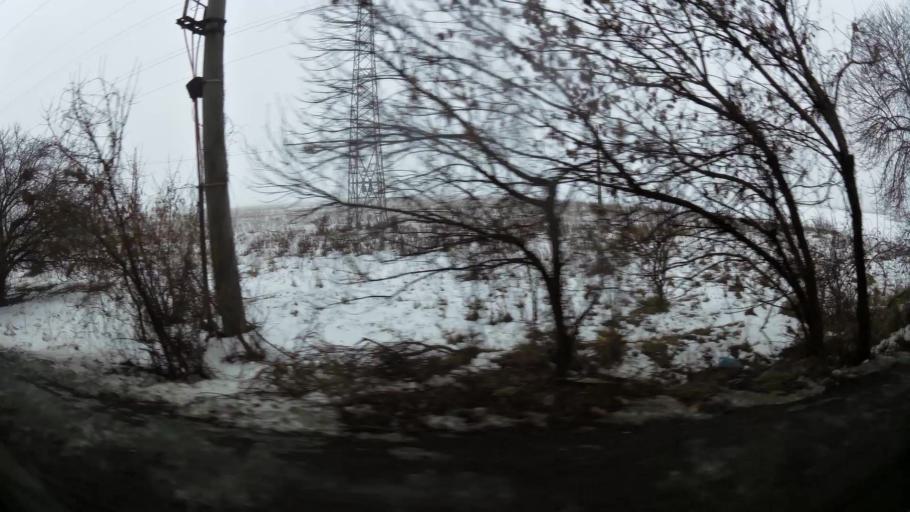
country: RO
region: Ilfov
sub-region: Comuna Chiajna
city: Chiajna
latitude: 44.4276
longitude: 25.9674
